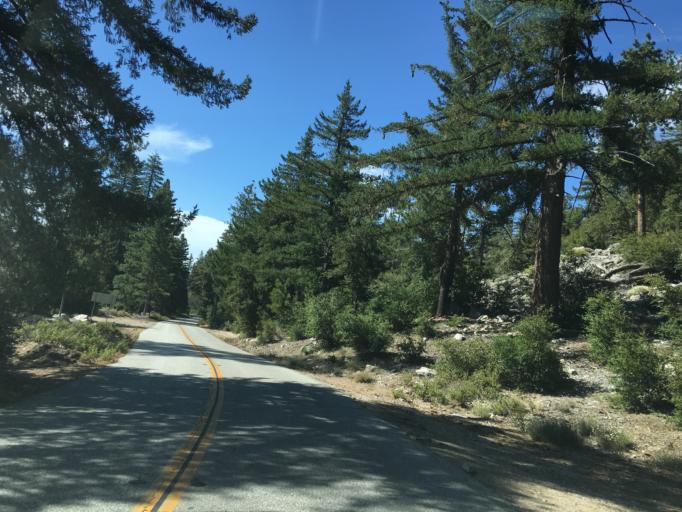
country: US
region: California
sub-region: Los Angeles County
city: Glendora
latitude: 34.3188
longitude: -117.8436
